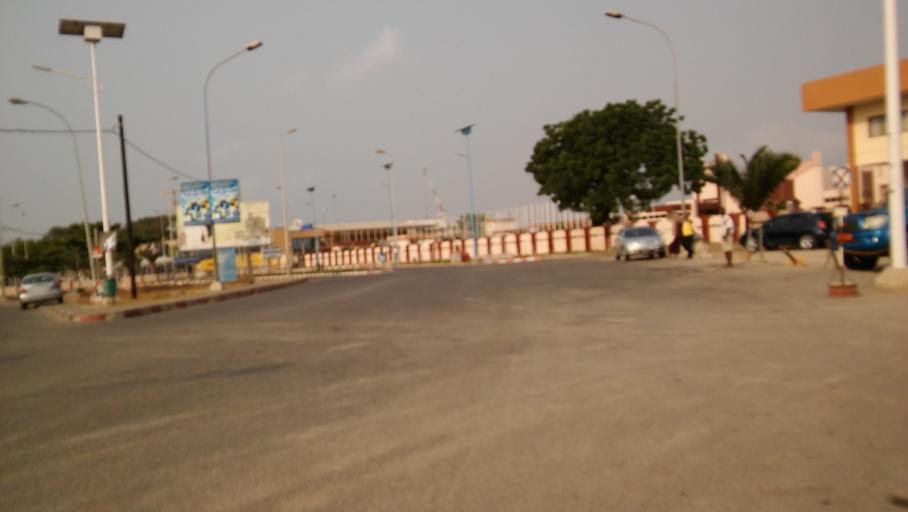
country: BJ
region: Littoral
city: Cotonou
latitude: 6.3539
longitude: 2.3869
